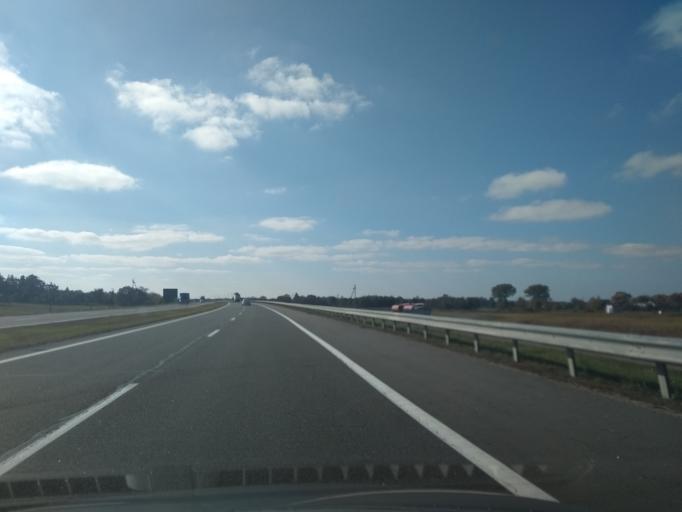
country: BY
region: Brest
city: Baranovichi
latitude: 53.1359
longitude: 25.9236
